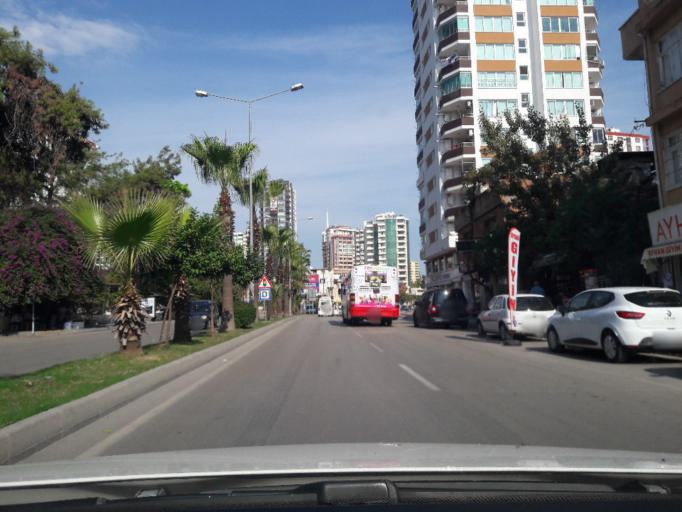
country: TR
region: Adana
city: Adana
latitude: 37.0211
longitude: 35.3196
